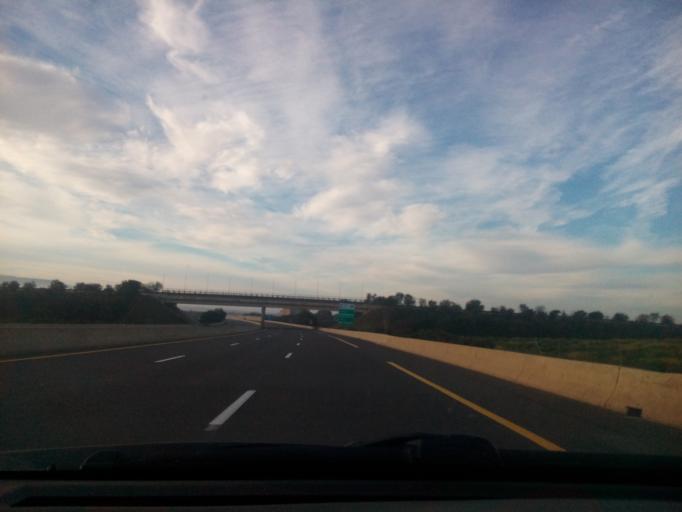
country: DZ
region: Relizane
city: Relizane
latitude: 35.7312
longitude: 0.3048
